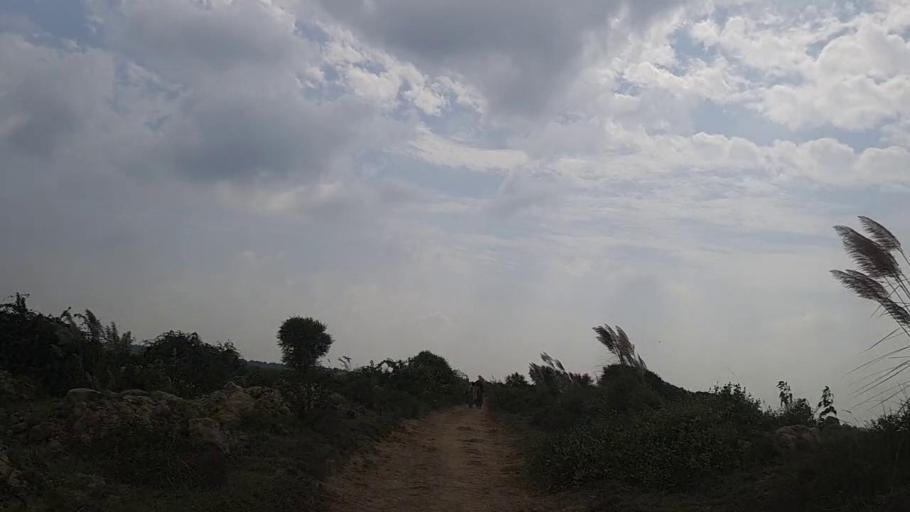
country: PK
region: Sindh
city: Mirpur Batoro
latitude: 24.6180
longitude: 68.1360
